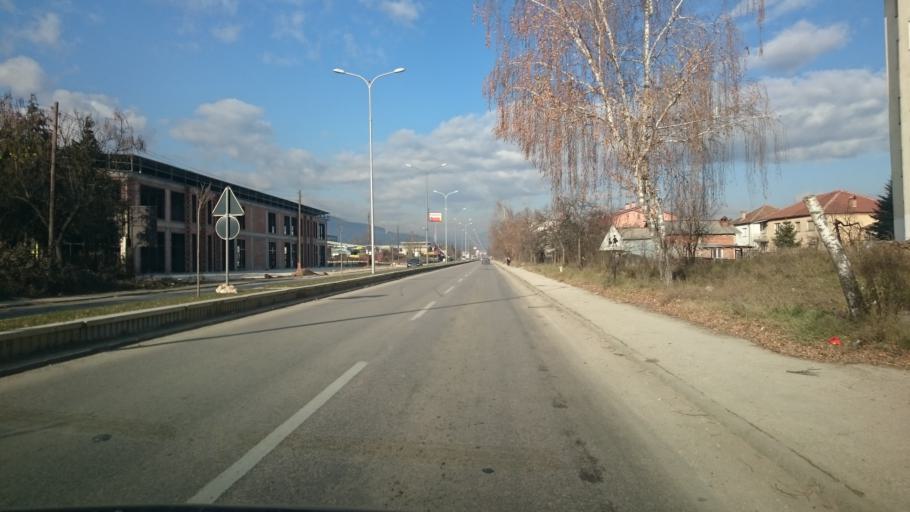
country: MK
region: Kicevo
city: Kicevo
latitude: 41.5077
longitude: 20.9525
